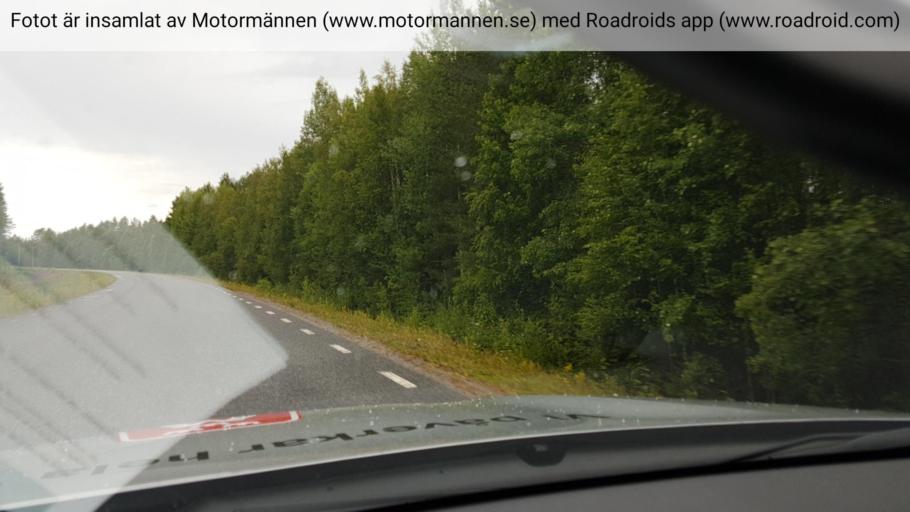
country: SE
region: Norrbotten
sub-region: Bodens Kommun
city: Boden
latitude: 65.8465
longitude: 21.4734
